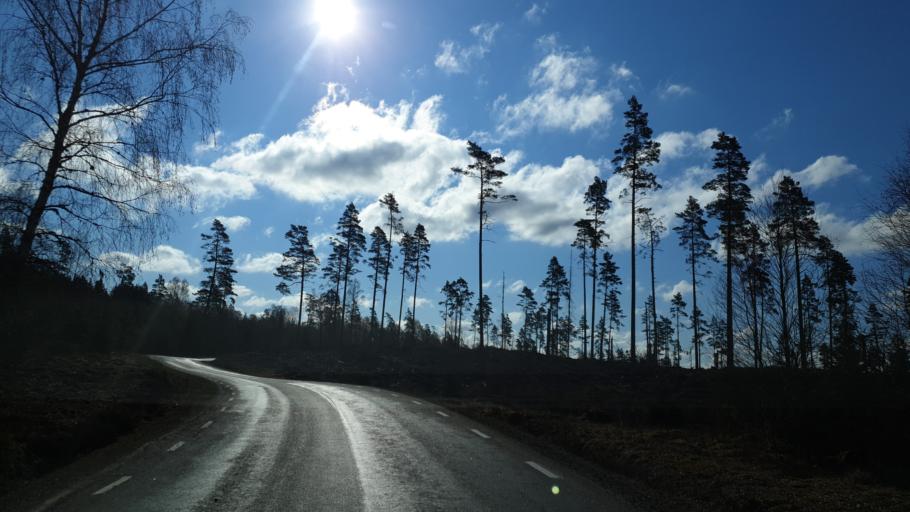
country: SE
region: Vaestra Goetaland
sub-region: Svenljunga Kommun
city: Svenljunga
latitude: 57.4471
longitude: 13.1146
